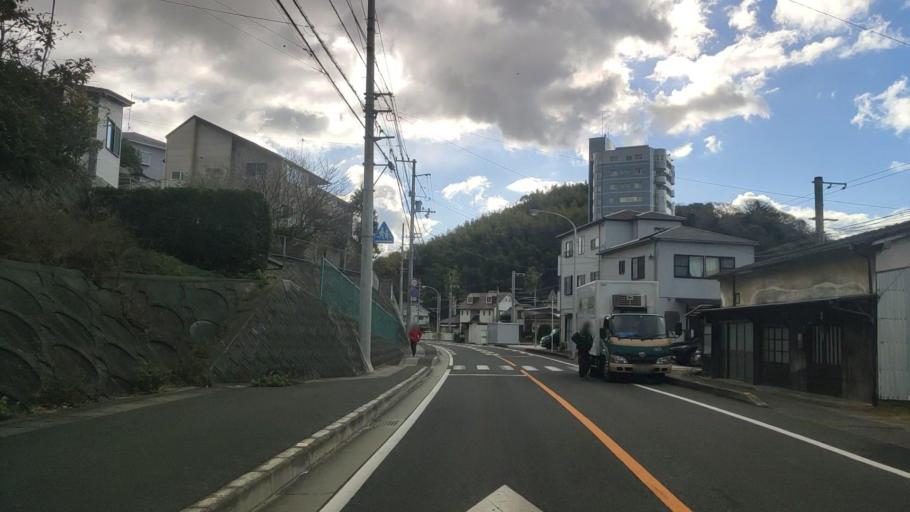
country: JP
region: Ehime
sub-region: Shikoku-chuo Shi
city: Matsuyama
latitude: 33.8709
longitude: 132.7103
